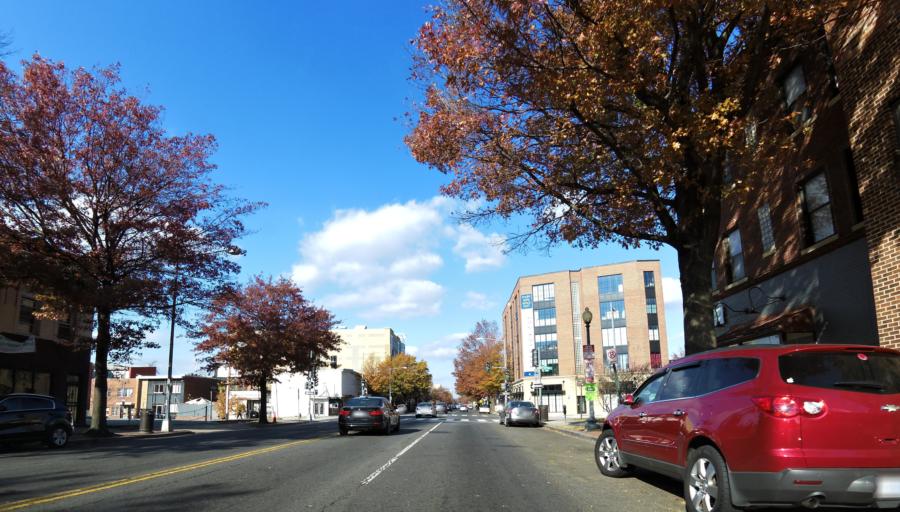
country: US
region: Washington, D.C.
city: Washington, D.C.
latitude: 38.9295
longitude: -77.0233
